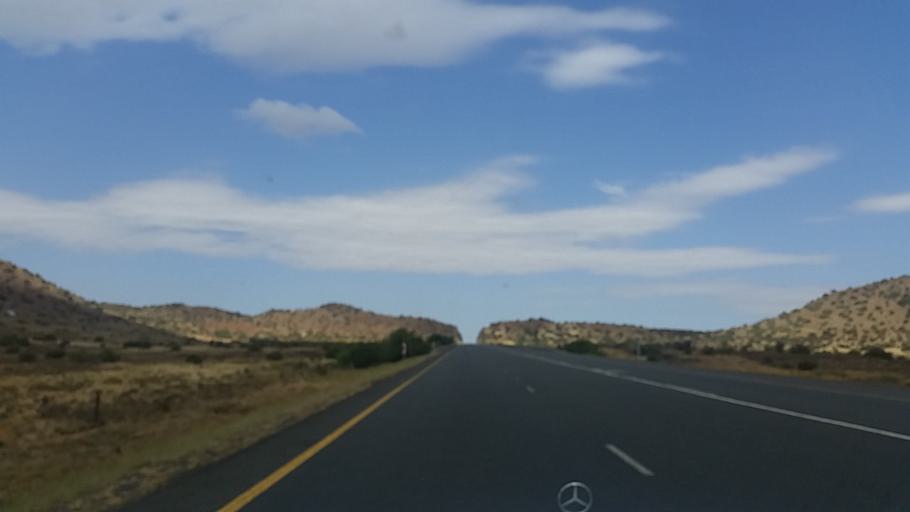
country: ZA
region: Northern Cape
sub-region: Pixley ka Seme District Municipality
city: Colesberg
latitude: -30.6408
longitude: 25.2261
